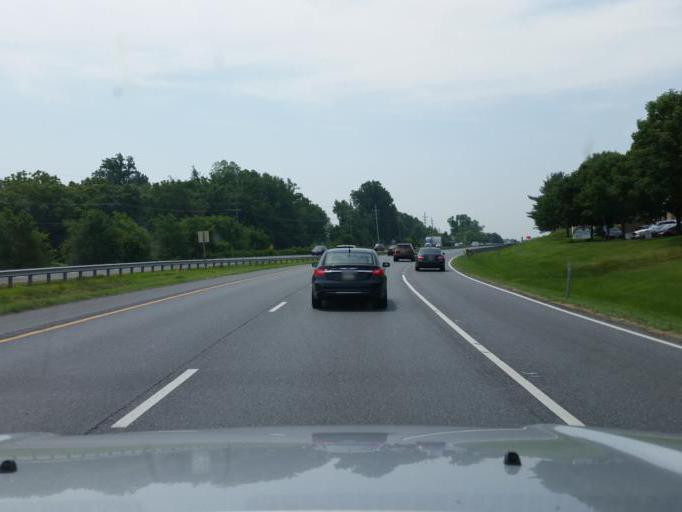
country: US
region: Maryland
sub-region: Frederick County
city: Clover Hill
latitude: 39.4551
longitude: -77.3995
